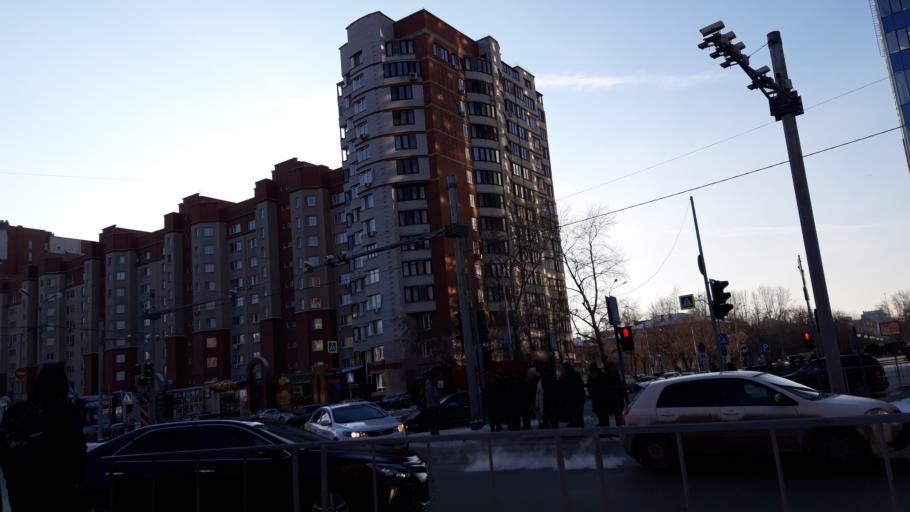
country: RU
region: Tjumen
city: Tyumen
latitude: 57.1527
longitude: 65.5683
